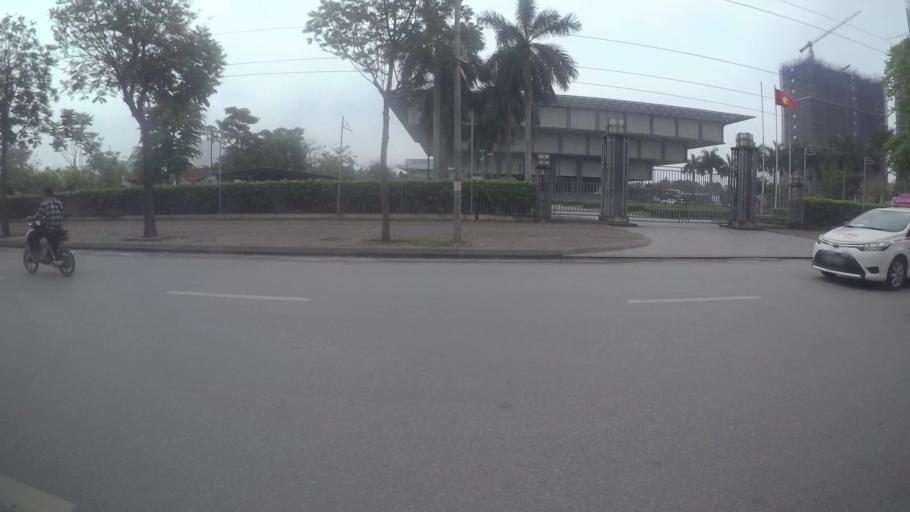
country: VN
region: Ha Noi
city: Thanh Xuan
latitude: 21.0105
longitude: 105.7876
